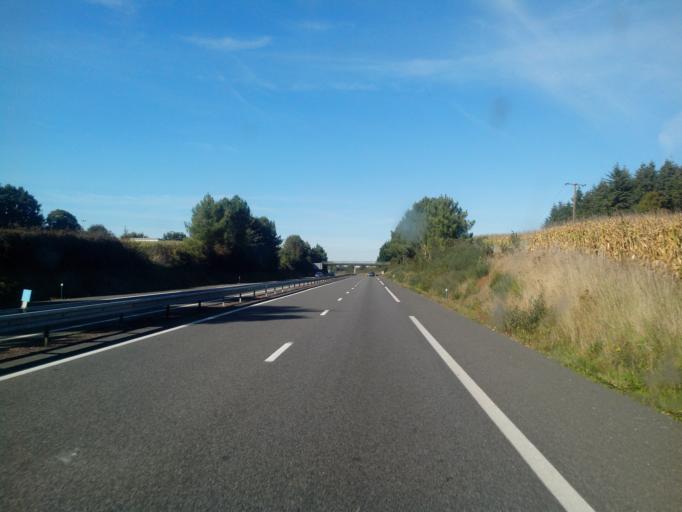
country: FR
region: Brittany
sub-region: Departement du Morbihan
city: Malestroit
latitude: 47.8602
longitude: -2.4172
